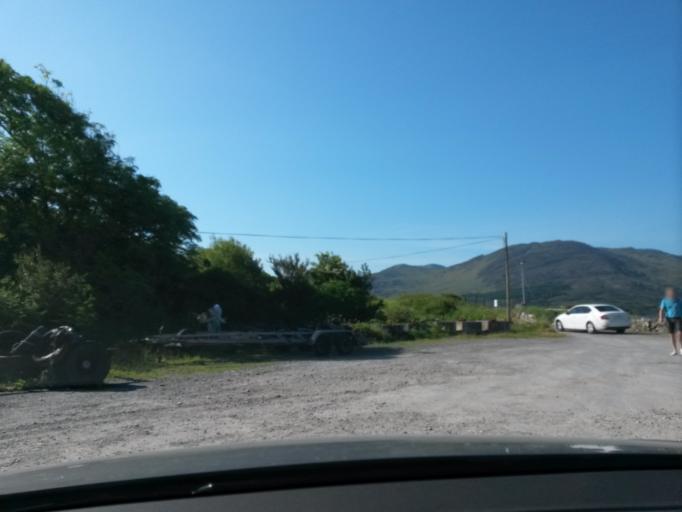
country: IE
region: Munster
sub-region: Ciarrai
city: Kenmare
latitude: 51.7804
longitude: -9.8052
